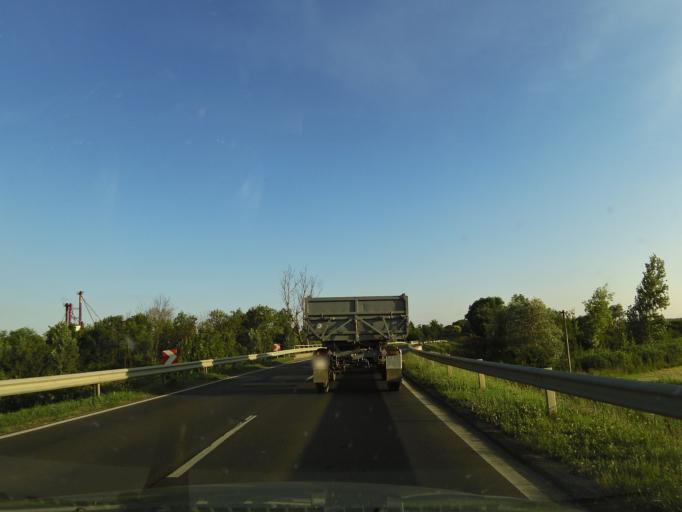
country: HU
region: Csongrad
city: Szentes
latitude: 46.6969
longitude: 20.3261
